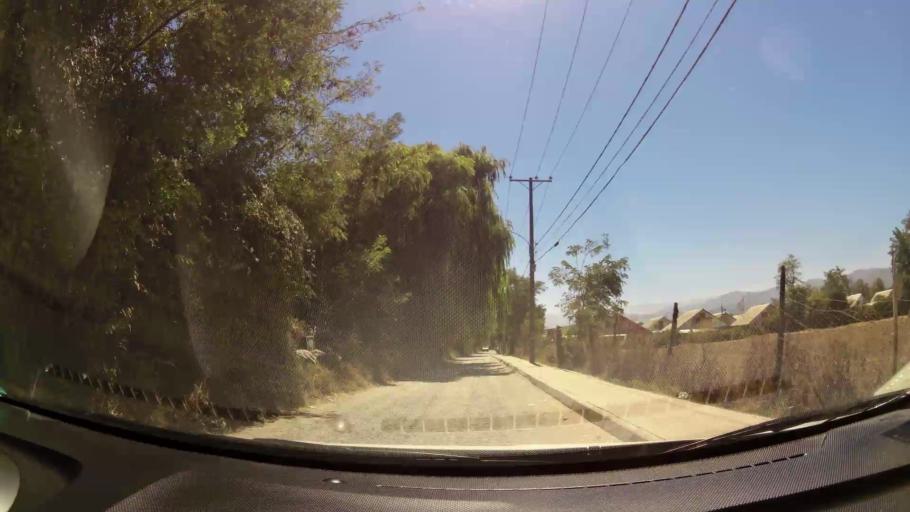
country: CL
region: O'Higgins
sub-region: Provincia de Cachapoal
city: Rancagua
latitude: -34.1464
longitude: -70.7234
